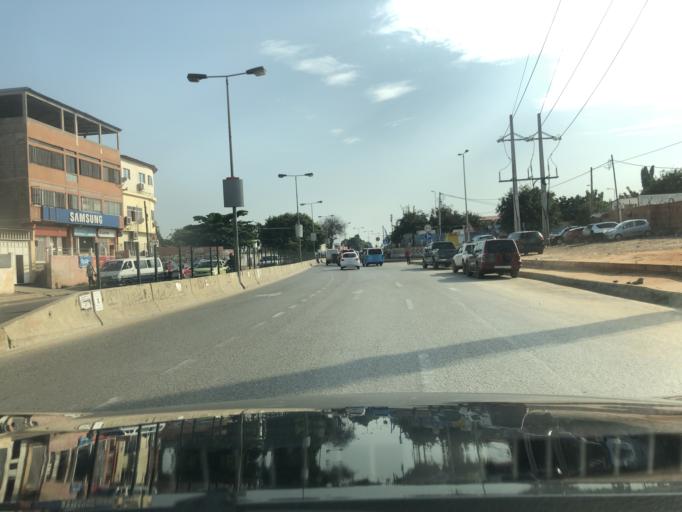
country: AO
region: Luanda
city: Luanda
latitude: -8.8432
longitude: 13.2403
